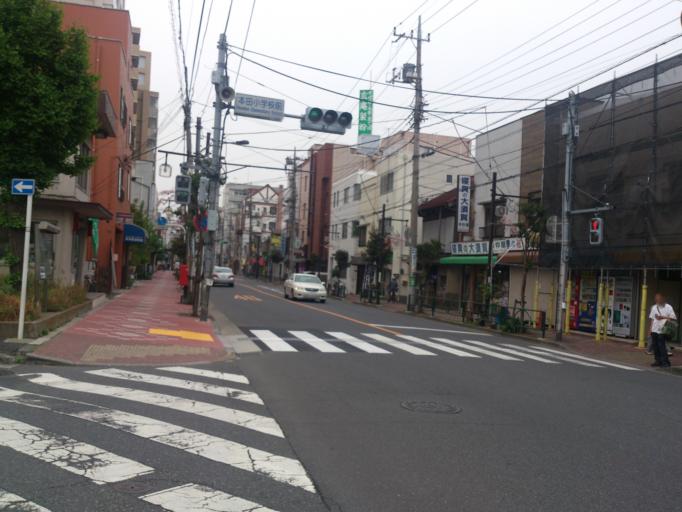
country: JP
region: Chiba
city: Matsudo
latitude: 35.7365
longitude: 139.8452
